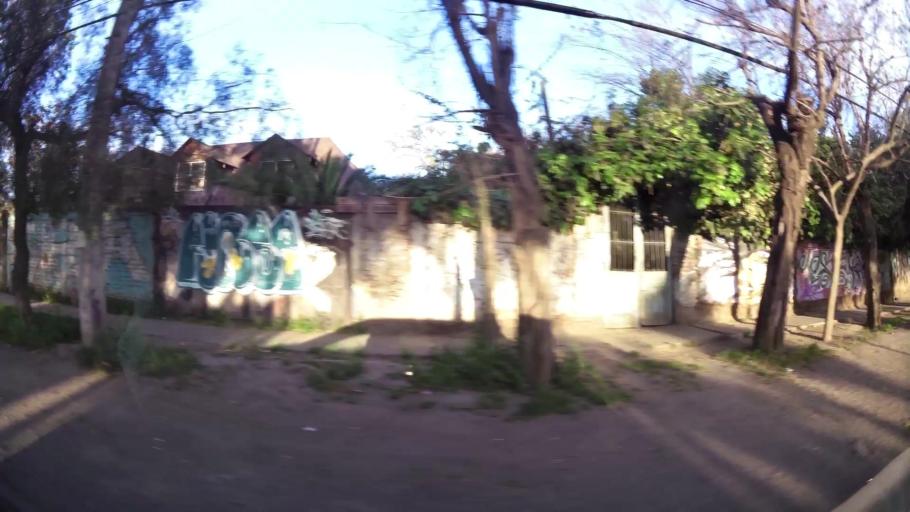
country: CL
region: Santiago Metropolitan
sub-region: Provincia de Santiago
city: Lo Prado
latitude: -33.4333
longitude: -70.7208
